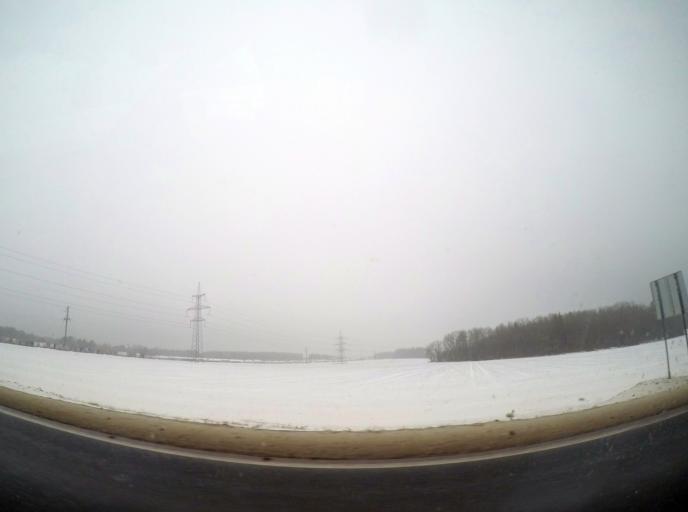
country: BY
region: Grodnenskaya
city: Hrodna
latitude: 53.6205
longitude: 23.8749
